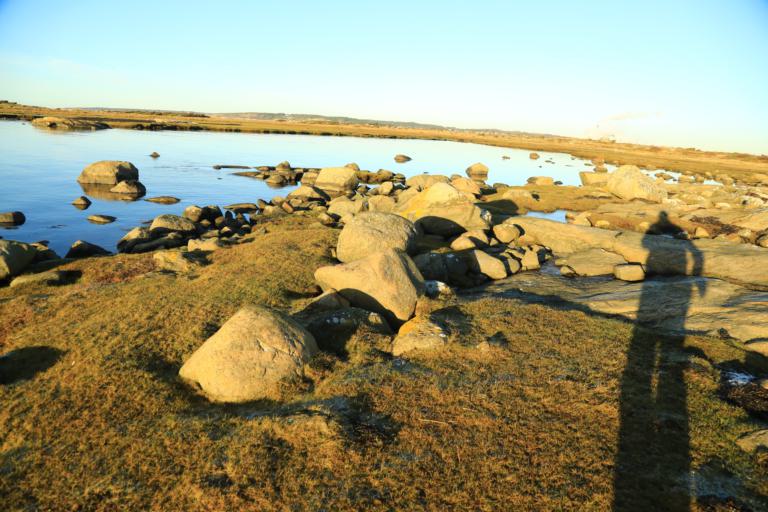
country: SE
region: Halland
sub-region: Kungsbacka Kommun
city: Frillesas
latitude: 57.1933
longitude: 12.1574
